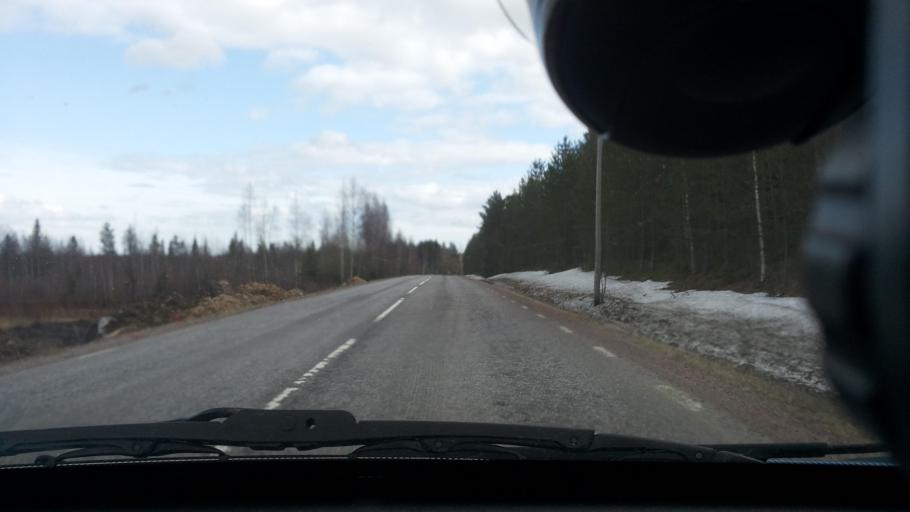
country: SE
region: Norrbotten
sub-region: Lulea Kommun
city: Sodra Sunderbyn
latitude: 65.6604
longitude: 21.8298
